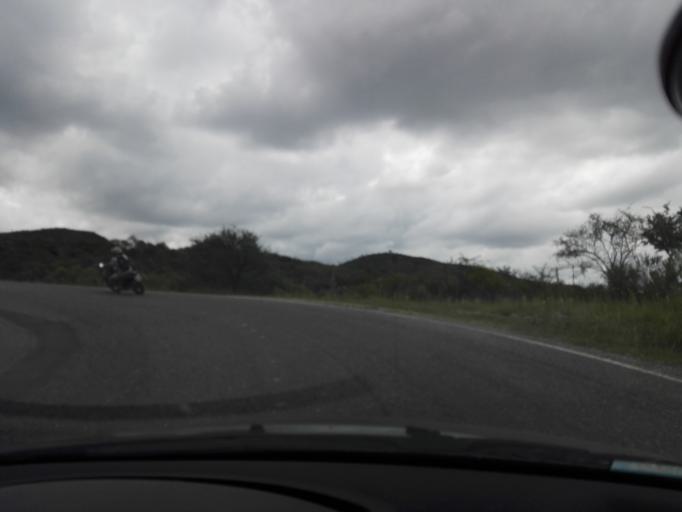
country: AR
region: Cordoba
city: Alta Gracia
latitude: -31.5899
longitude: -64.5021
